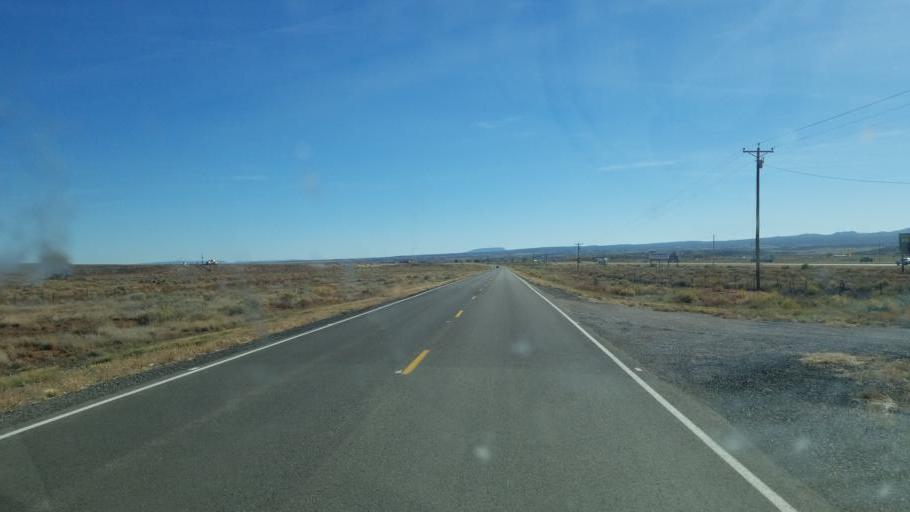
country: US
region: New Mexico
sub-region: Cibola County
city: Milan
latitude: 35.2943
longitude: -107.9868
